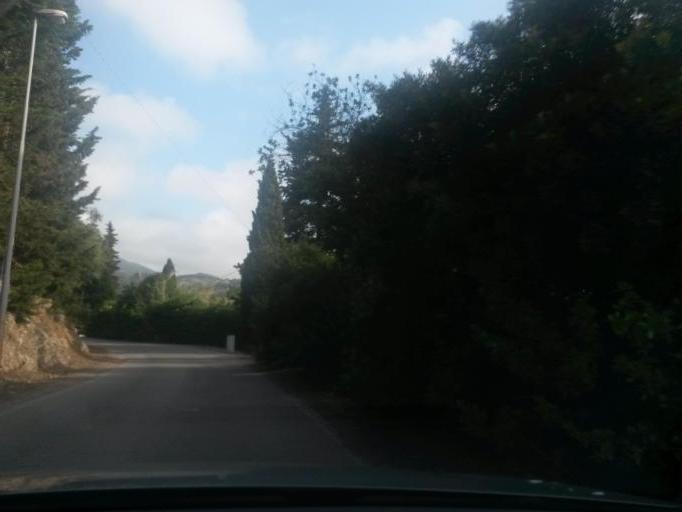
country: IT
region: Tuscany
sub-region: Provincia di Livorno
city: Porto Azzurro
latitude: 42.7755
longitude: 10.4137
